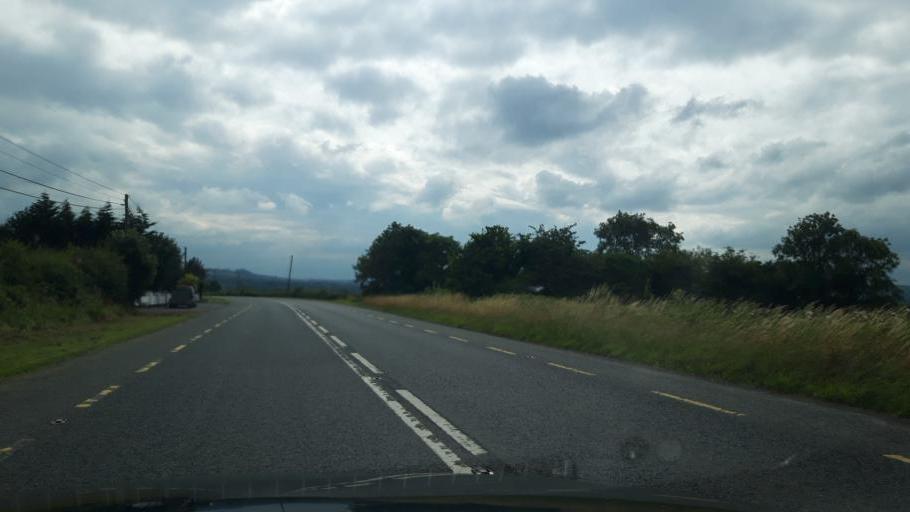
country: IE
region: Leinster
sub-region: Kilkenny
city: Castlecomer
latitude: 52.8567
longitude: -7.1161
